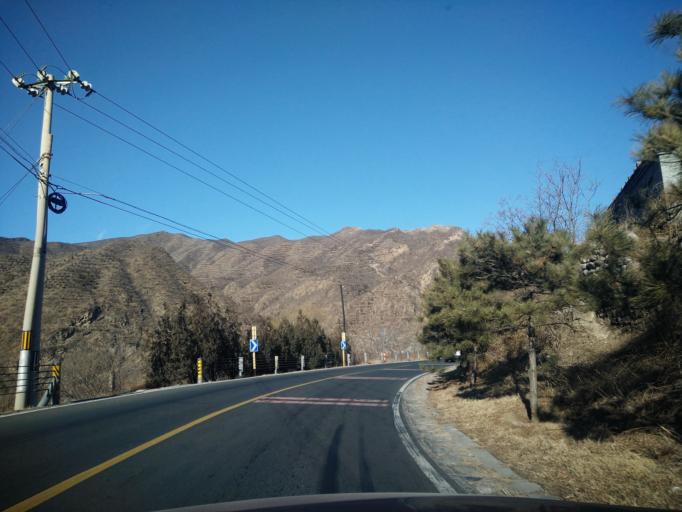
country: CN
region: Beijing
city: Yanchi
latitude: 40.0195
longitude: 115.8654
